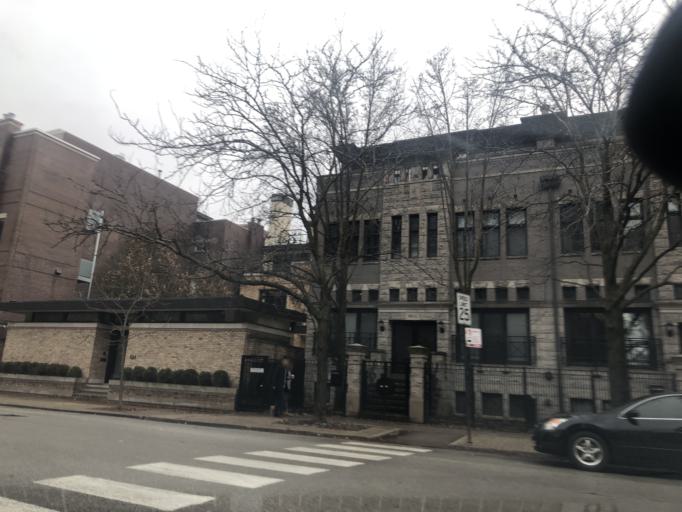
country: US
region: Illinois
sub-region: Cook County
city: Chicago
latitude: 41.8998
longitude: -87.6313
